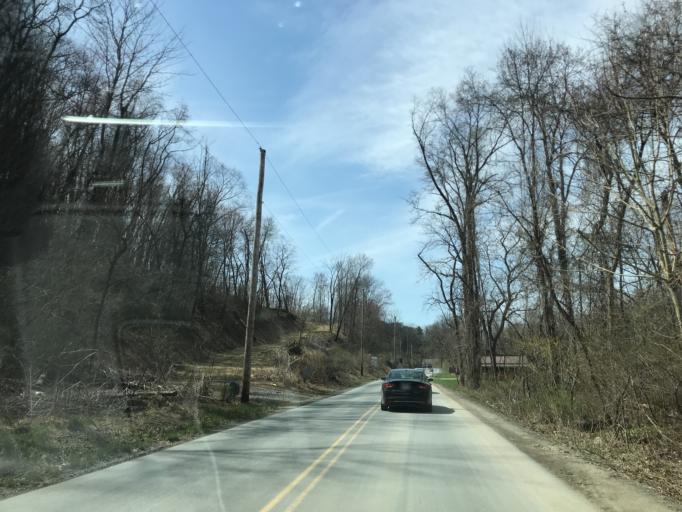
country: US
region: Pennsylvania
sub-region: Northumberland County
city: Northumberland
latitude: 40.8997
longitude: -76.8407
